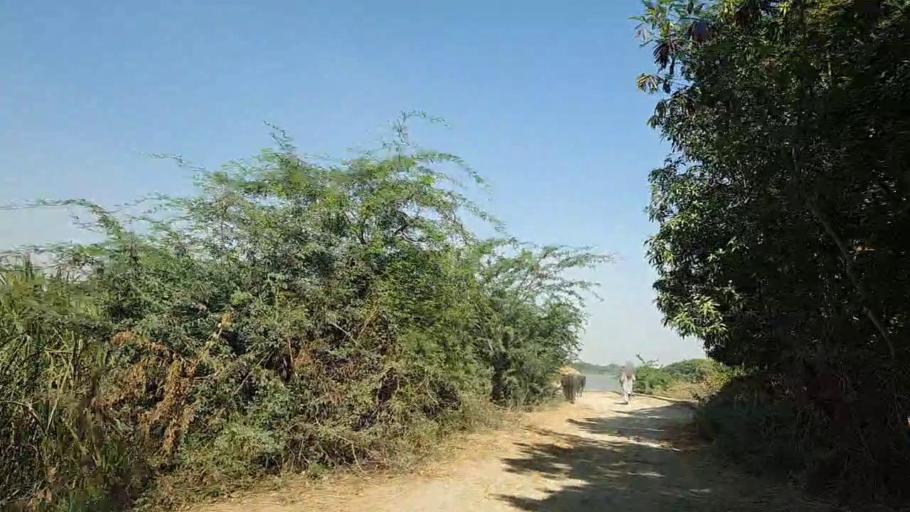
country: PK
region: Sindh
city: Daro Mehar
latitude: 24.8150
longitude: 68.1869
